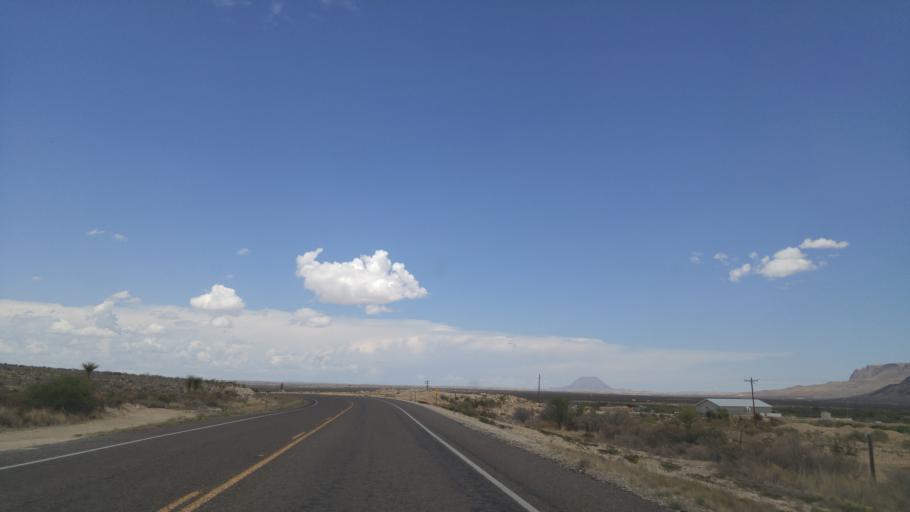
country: US
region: Texas
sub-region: Brewster County
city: Alpine
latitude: 29.5964
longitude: -103.5602
